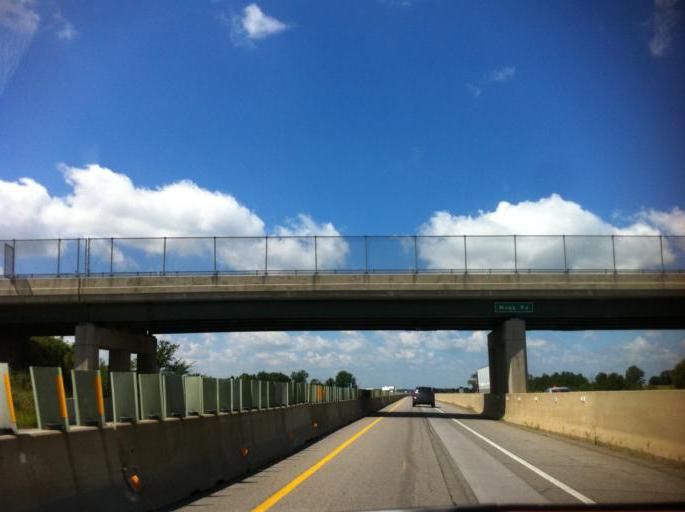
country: US
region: Ohio
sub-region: Sandusky County
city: Clyde
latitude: 41.3602
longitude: -82.9160
